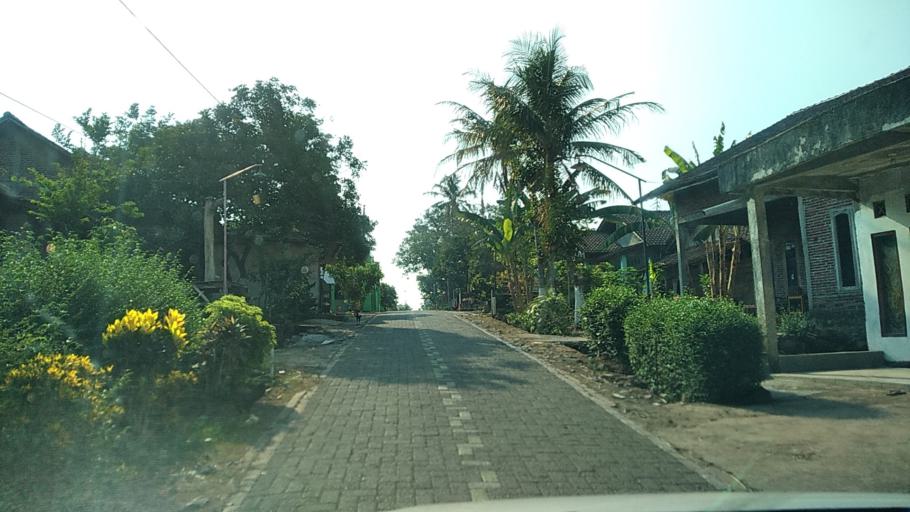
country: ID
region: Central Java
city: Semarang
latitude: -7.0256
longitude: 110.3058
